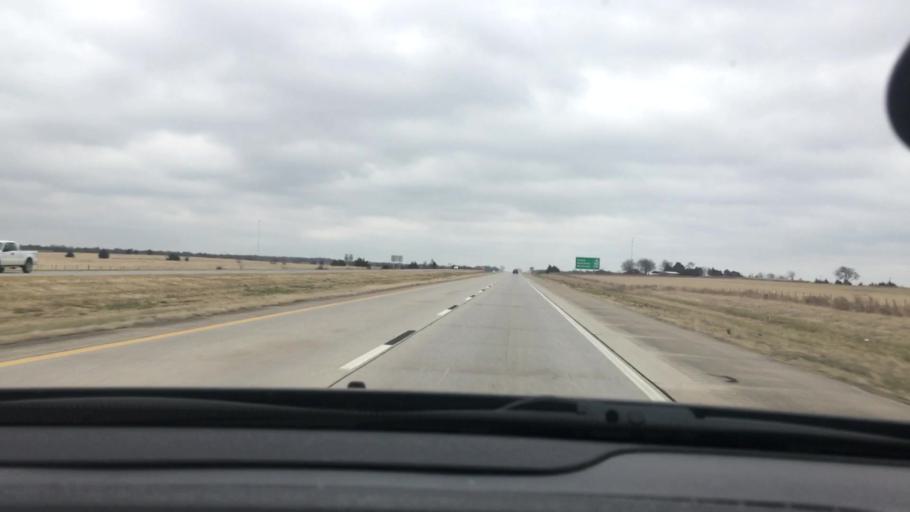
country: US
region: Oklahoma
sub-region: Bryan County
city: Durant
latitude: 34.1524
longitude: -96.2618
